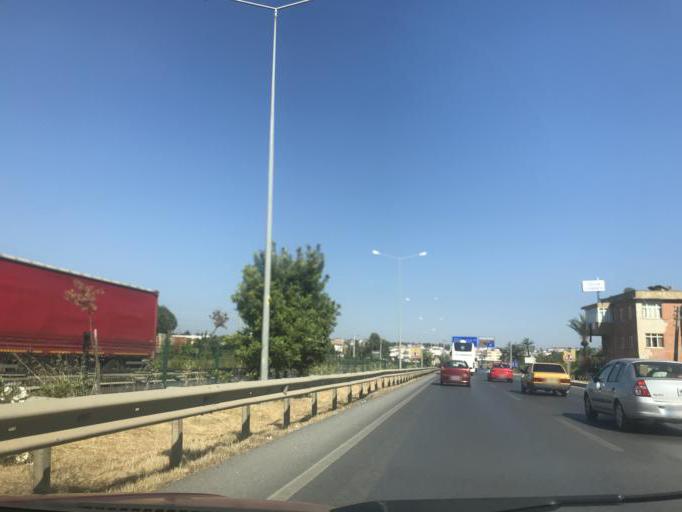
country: TR
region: Antalya
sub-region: Manavgat
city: Side
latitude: 36.7994
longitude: 31.4041
